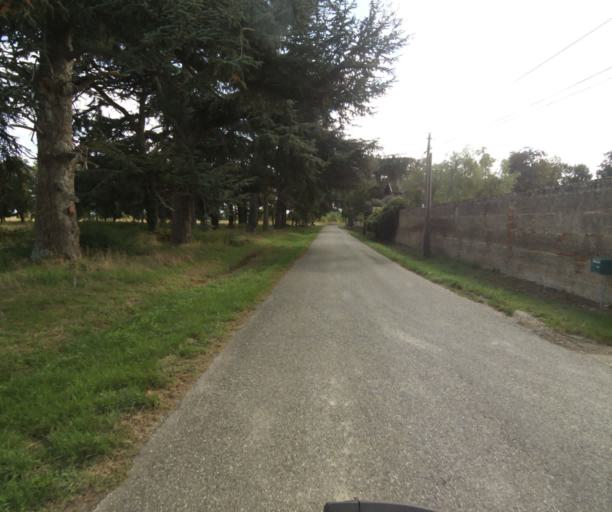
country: FR
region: Midi-Pyrenees
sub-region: Departement du Tarn-et-Garonne
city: Finhan
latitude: 43.9285
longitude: 1.2174
